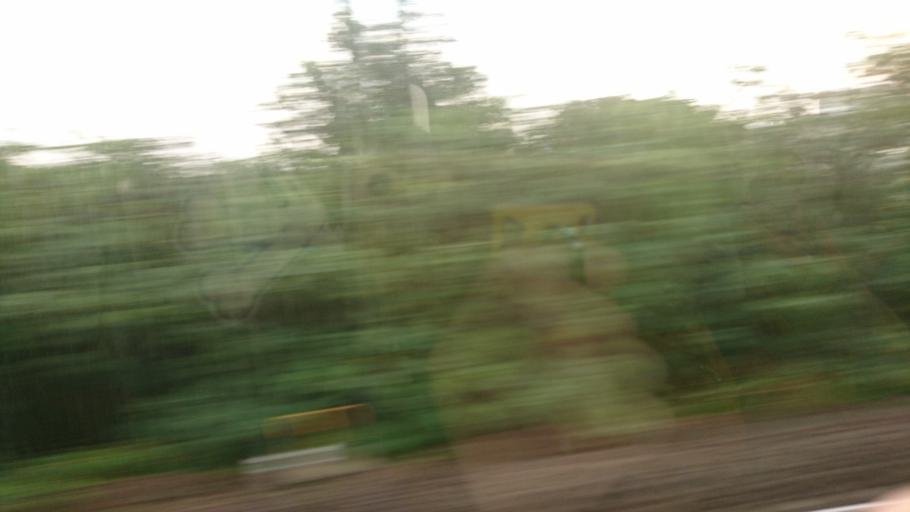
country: TW
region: Taiwan
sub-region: Hsinchu
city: Hsinchu
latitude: 24.8131
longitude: 120.9917
